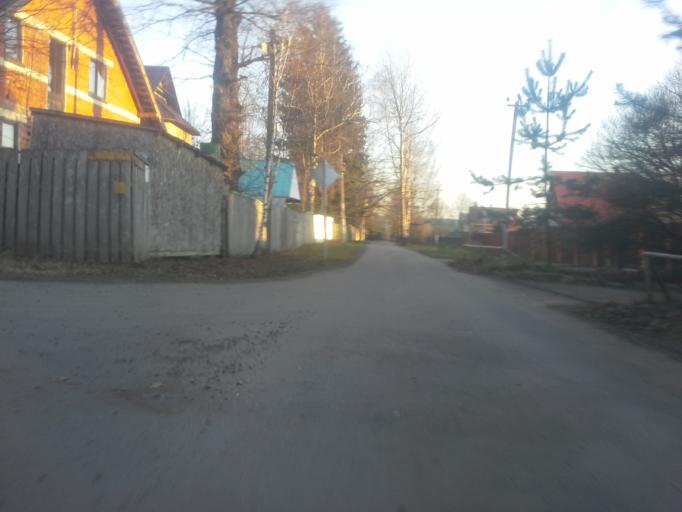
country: RU
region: Moskovskaya
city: Lesnoy Gorodok
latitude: 55.6322
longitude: 37.2060
